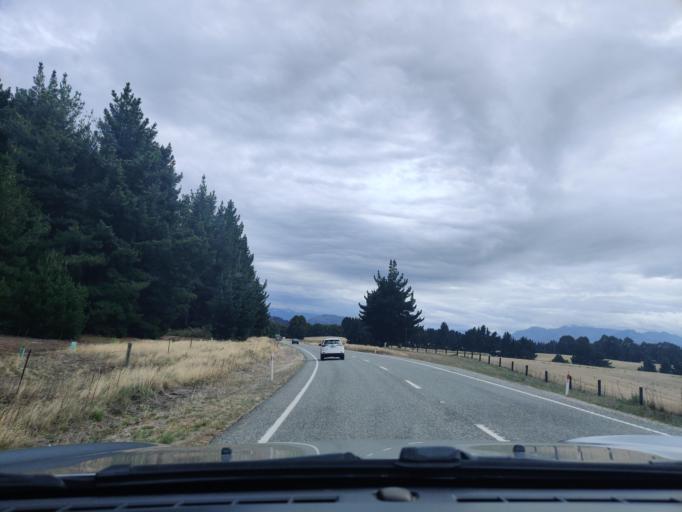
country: NZ
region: Otago
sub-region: Queenstown-Lakes District
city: Wanaka
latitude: -44.7103
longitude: 169.2070
